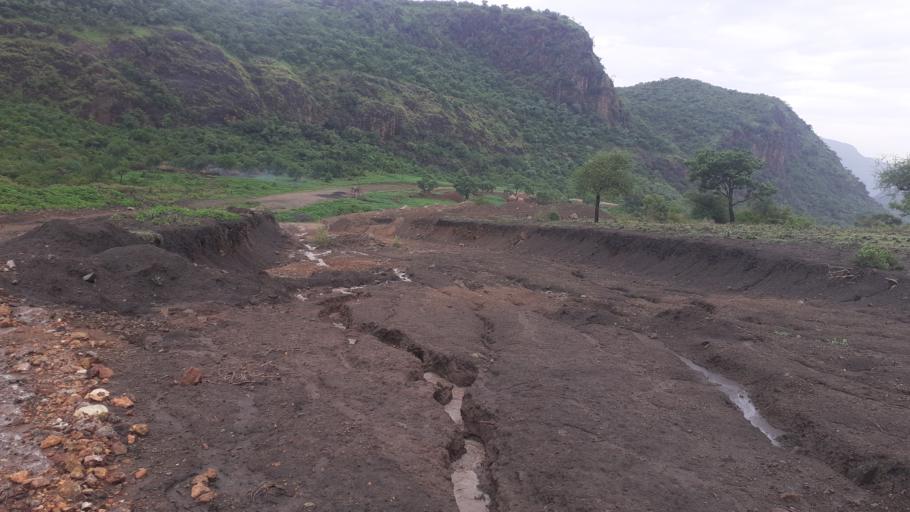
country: ET
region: Southern Nations, Nationalities, and People's Region
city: Areka
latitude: 7.6010
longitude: 37.5195
